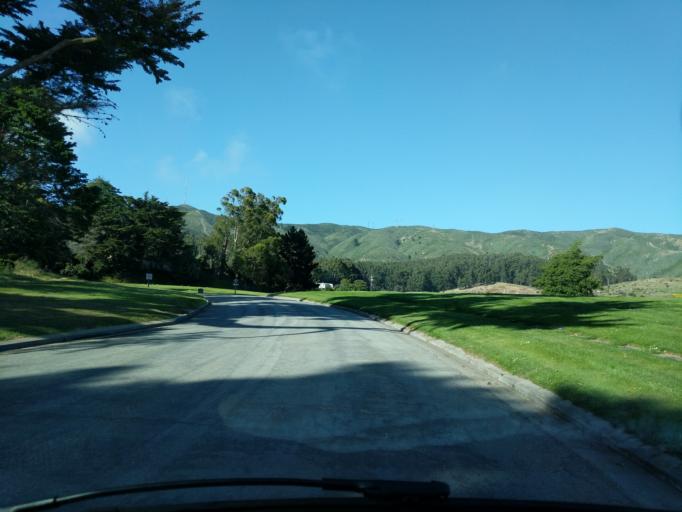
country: US
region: California
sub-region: San Mateo County
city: Colma
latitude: 37.6720
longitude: -122.4411
